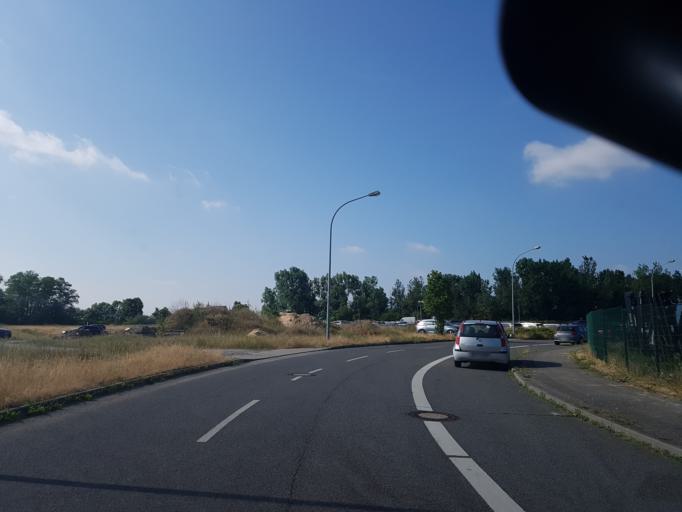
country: DE
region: Brandenburg
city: Juterbog
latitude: 52.0087
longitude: 13.0913
